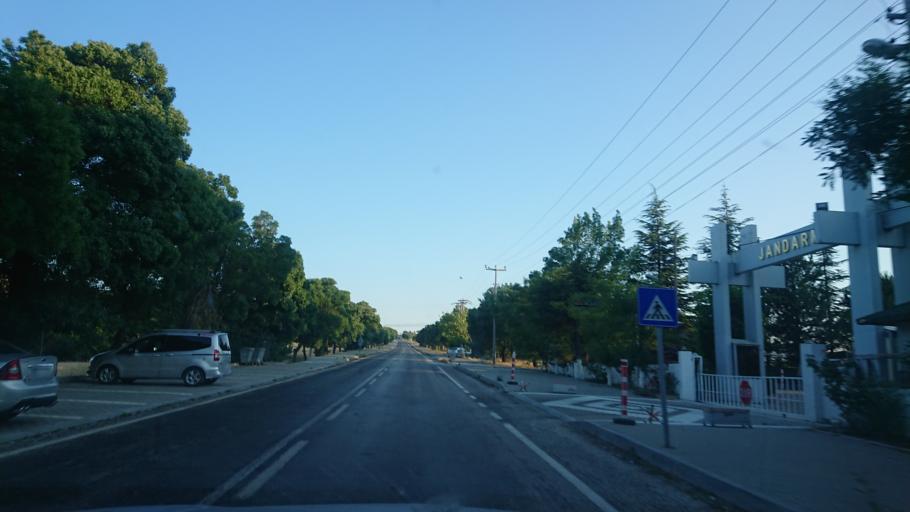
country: TR
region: Aksaray
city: Sariyahsi
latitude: 38.9665
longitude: 33.8393
